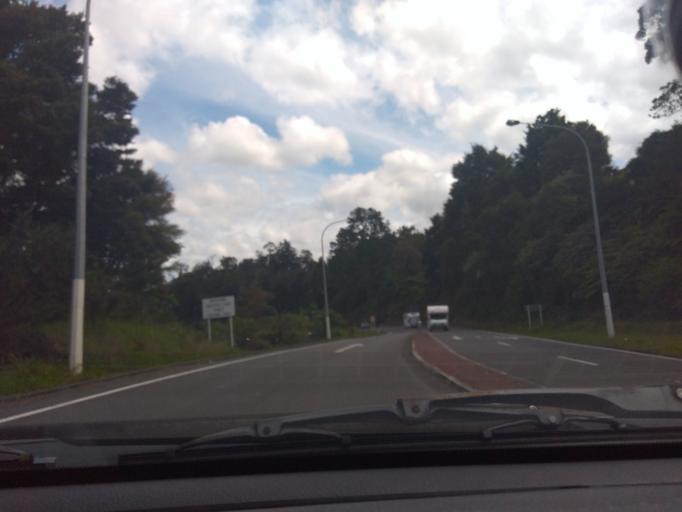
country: NZ
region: Northland
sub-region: Far North District
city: Kawakawa
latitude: -35.3811
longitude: 174.0717
